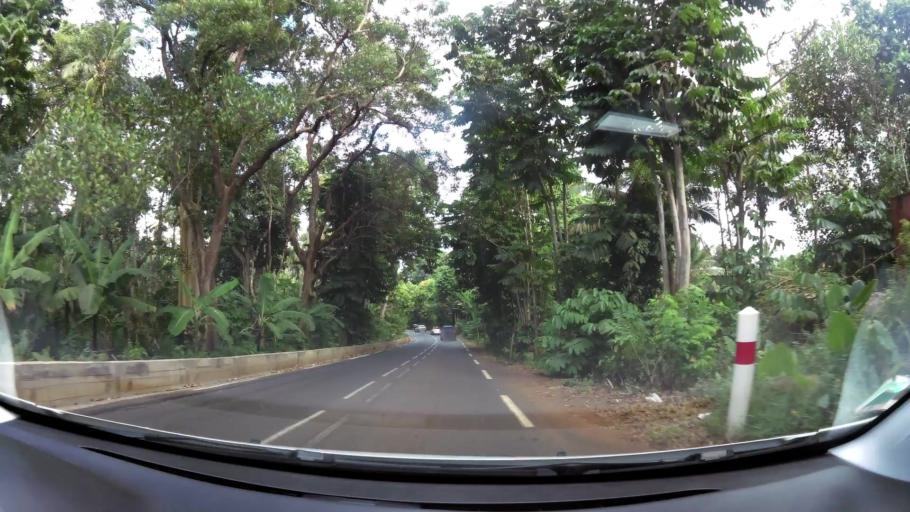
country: YT
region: Ouangani
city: Ouangani
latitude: -12.8371
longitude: 45.1566
